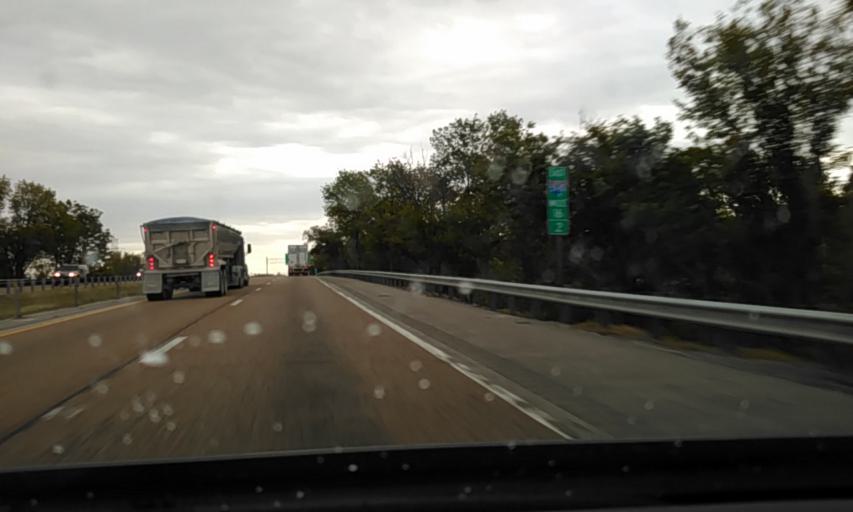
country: US
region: Illinois
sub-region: Madison County
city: Maryville
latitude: 38.7136
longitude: -89.9298
